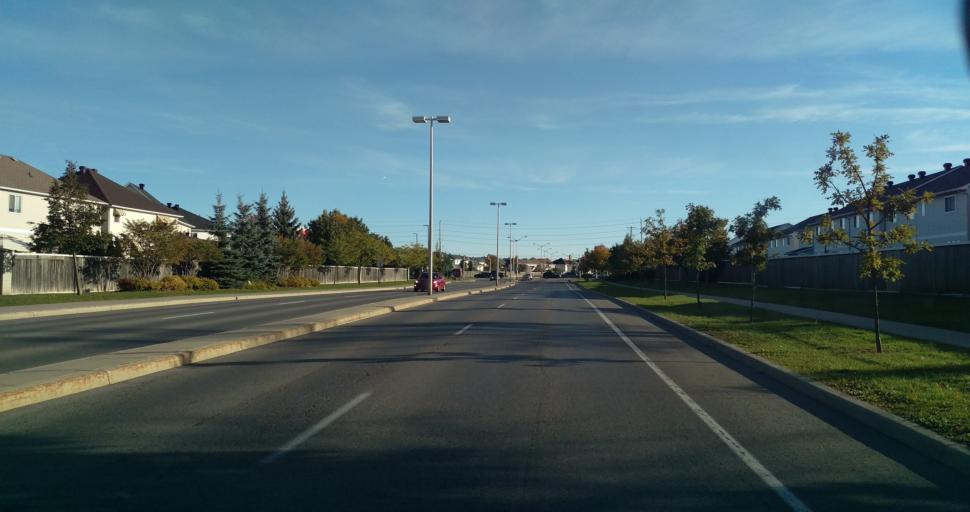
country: CA
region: Ontario
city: Clarence-Rockland
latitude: 45.4690
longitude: -75.4674
